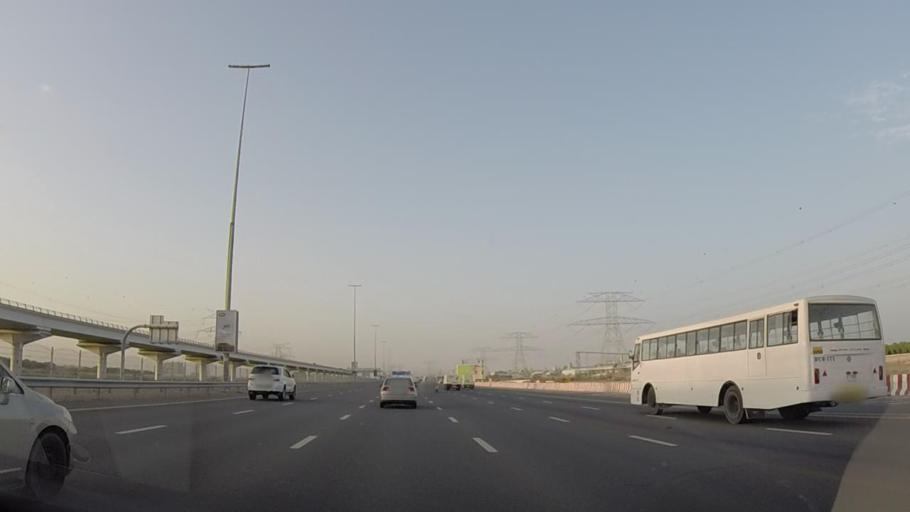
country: AE
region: Dubai
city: Dubai
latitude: 25.0381
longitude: 55.1091
